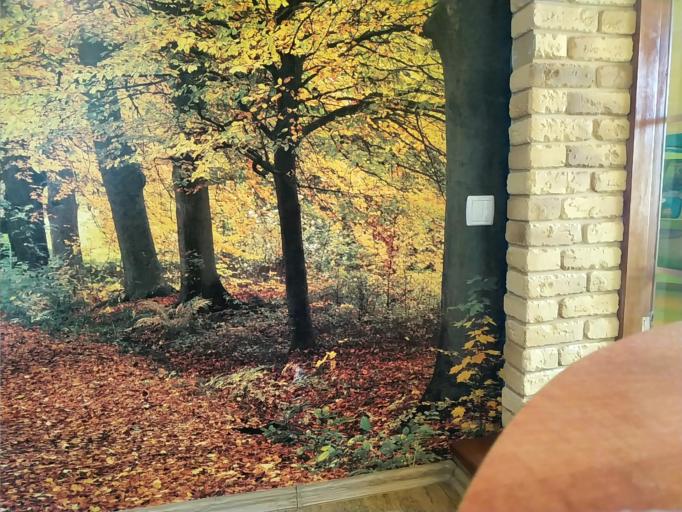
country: RU
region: Arkhangelskaya
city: Onega
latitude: 63.6963
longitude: 38.0903
